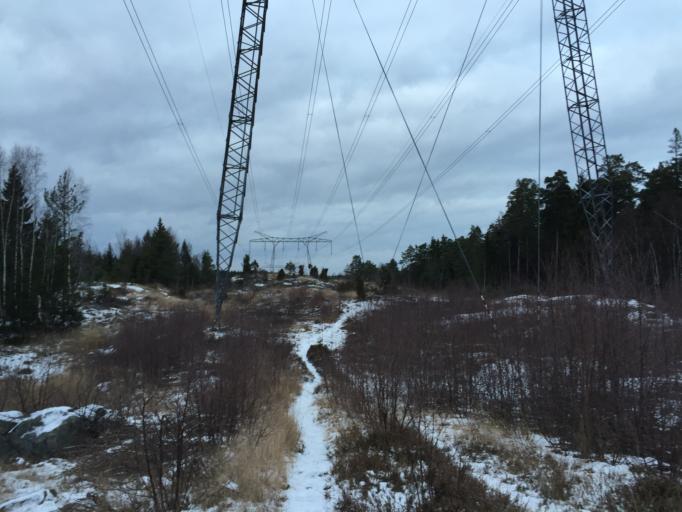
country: SE
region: Stockholm
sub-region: Salems Kommun
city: Ronninge
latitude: 59.2285
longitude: 17.6928
